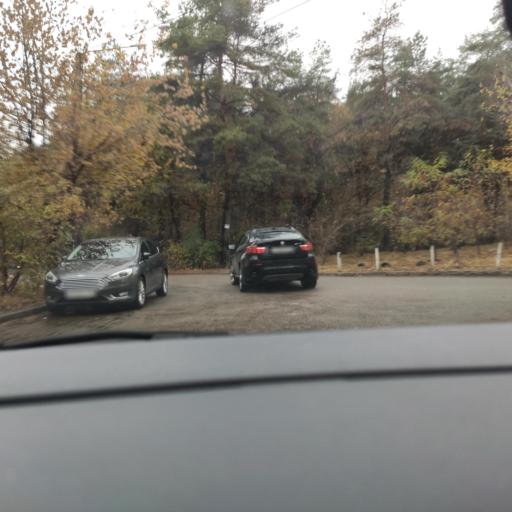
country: RU
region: Voronezj
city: Podgornoye
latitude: 51.6843
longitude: 39.1320
